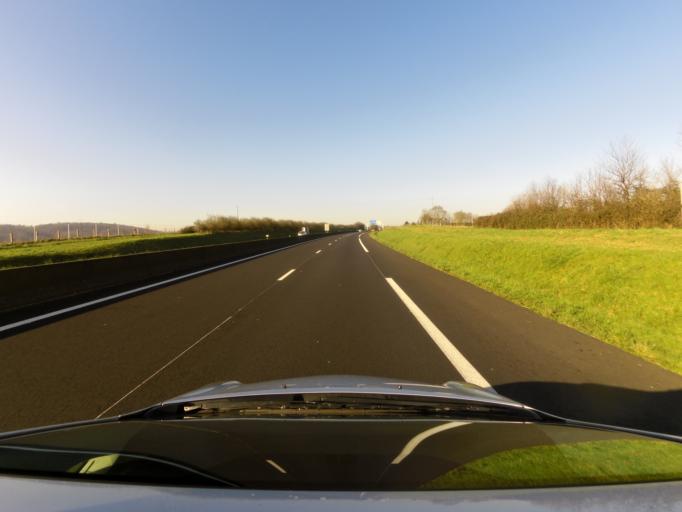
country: FR
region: Lower Normandy
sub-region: Departement du Calvados
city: Villers-Bocage
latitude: 49.0540
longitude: -0.7032
